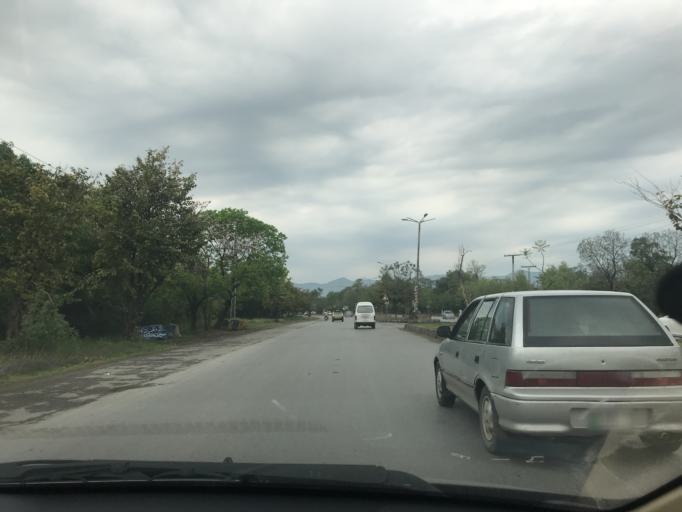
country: PK
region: Islamabad
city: Islamabad
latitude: 33.6848
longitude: 73.1352
